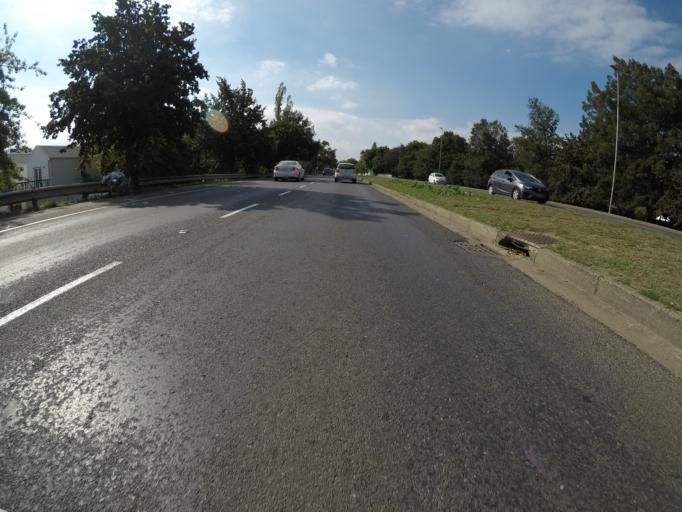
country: ZA
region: Western Cape
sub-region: Cape Winelands District Municipality
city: Stellenbosch
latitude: -33.9426
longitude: 18.8521
